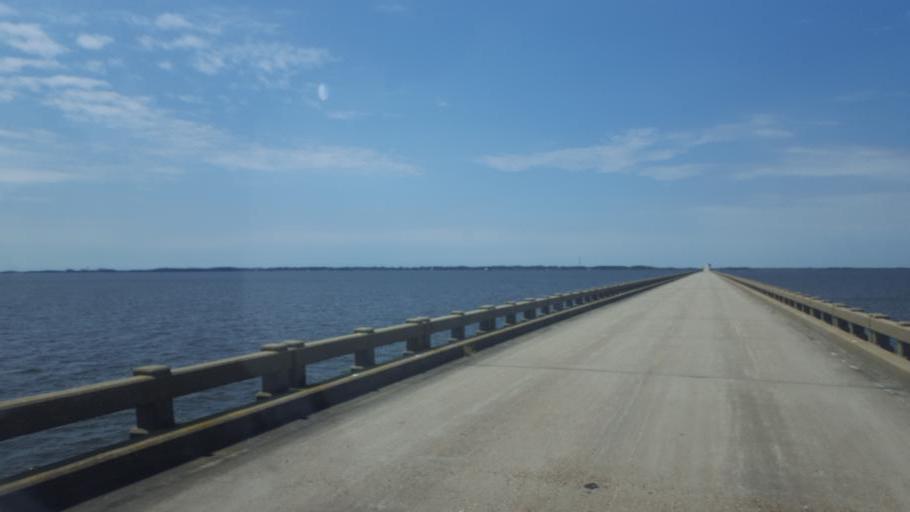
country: US
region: North Carolina
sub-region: Dare County
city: Manteo
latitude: 35.9238
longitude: -75.7336
